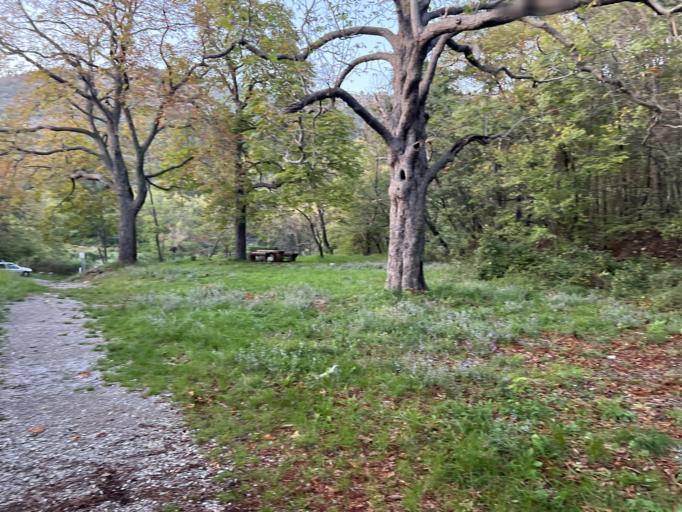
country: IT
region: Friuli Venezia Giulia
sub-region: Provincia di Trieste
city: Dolina
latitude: 45.6223
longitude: 13.8656
